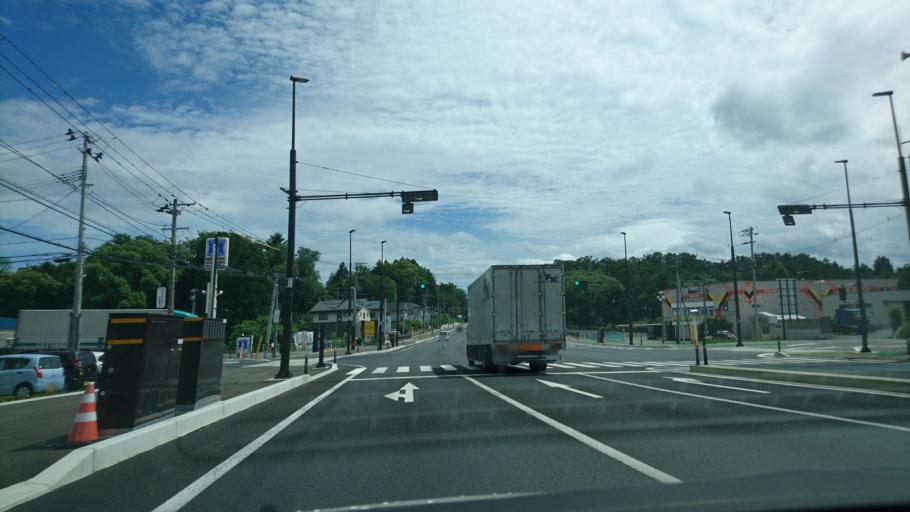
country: JP
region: Iwate
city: Morioka-shi
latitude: 39.7700
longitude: 141.1307
